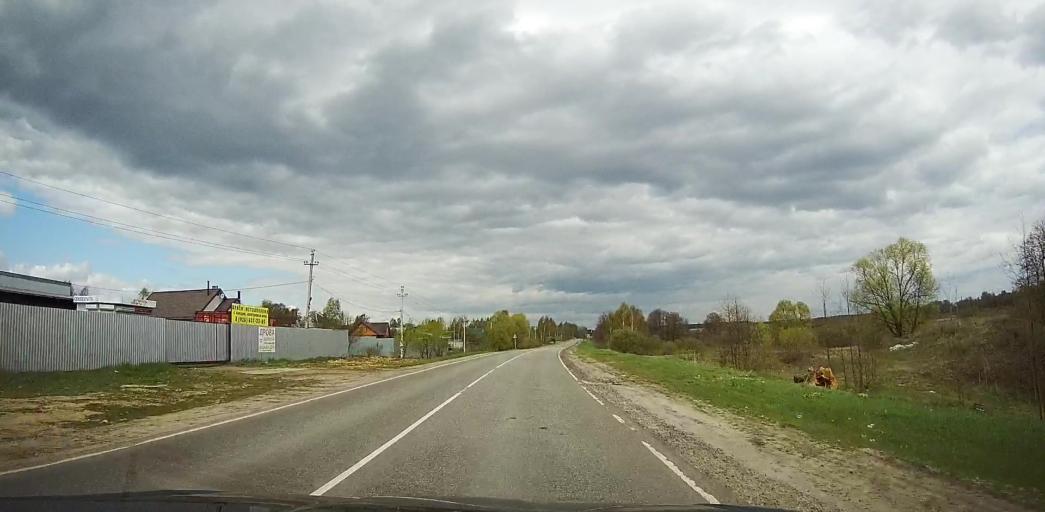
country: RU
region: Moskovskaya
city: Imeni Tsyurupy
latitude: 55.4876
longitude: 38.6196
